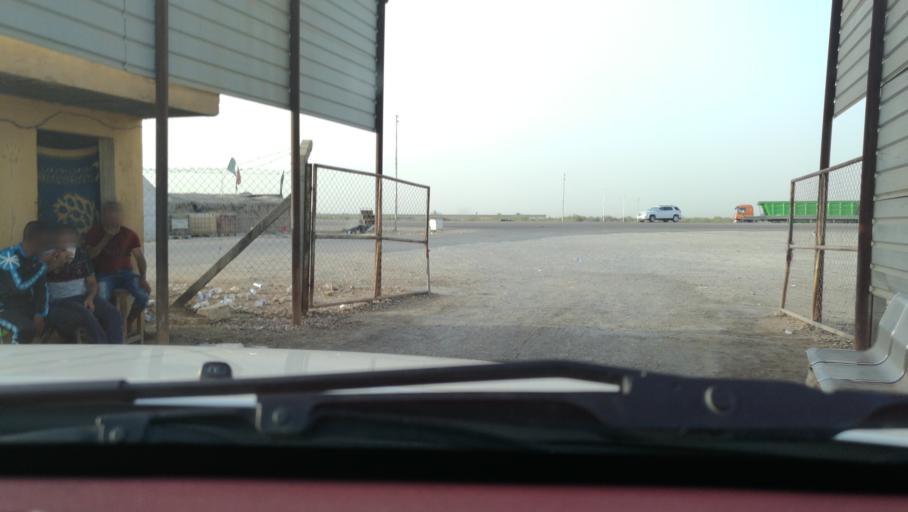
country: IQ
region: Babil
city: Imam Qasim
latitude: 32.2972
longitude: 44.8776
